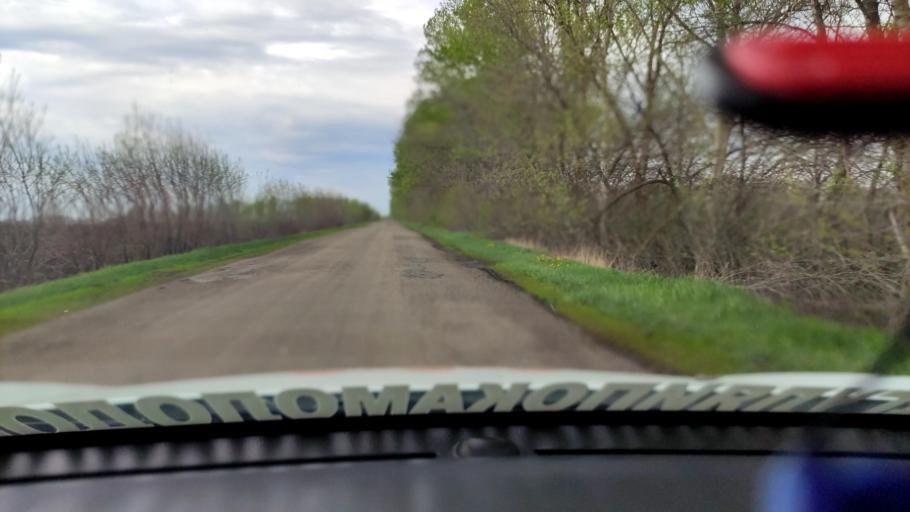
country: RU
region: Voronezj
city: Uryv-Pokrovka
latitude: 51.1279
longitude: 39.1094
